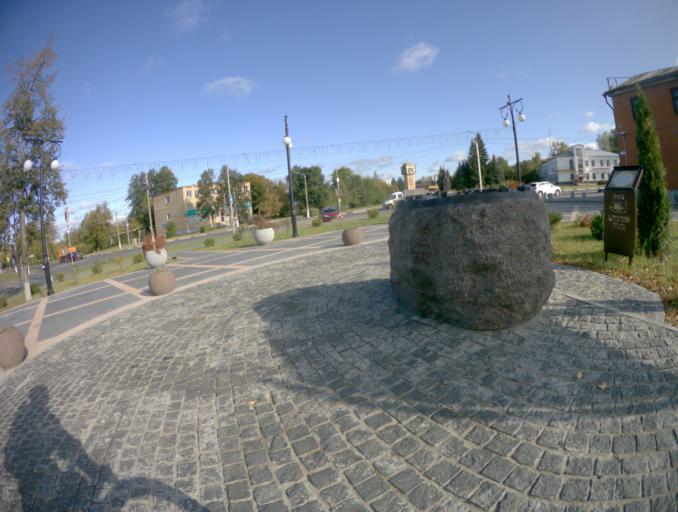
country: RU
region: Moskovskaya
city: Roshal'
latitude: 55.6621
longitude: 39.8689
